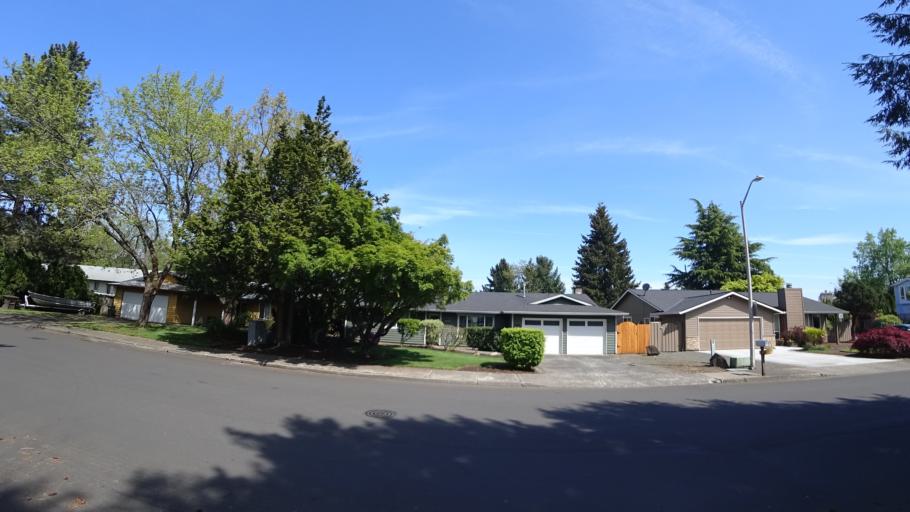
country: US
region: Oregon
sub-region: Washington County
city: Hillsboro
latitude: 45.5093
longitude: -122.9538
